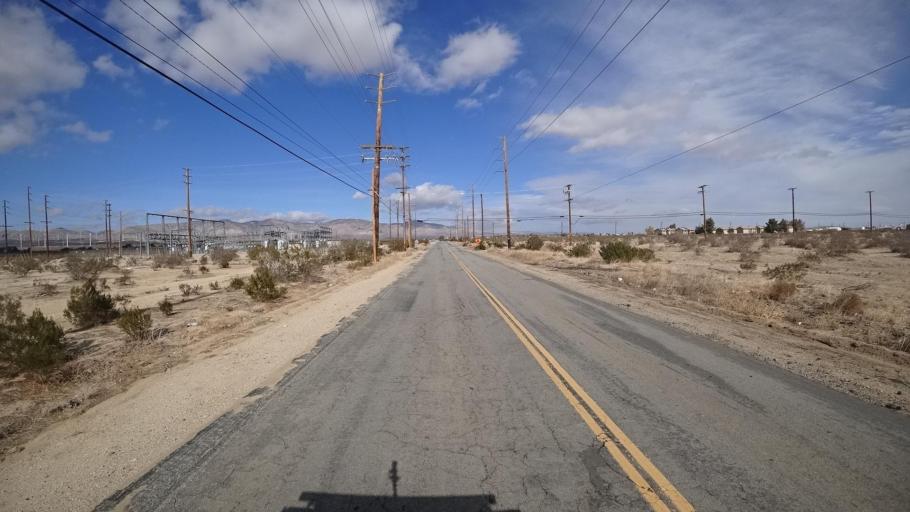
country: US
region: California
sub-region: Kern County
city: Mojave
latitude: 35.0532
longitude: -118.1855
